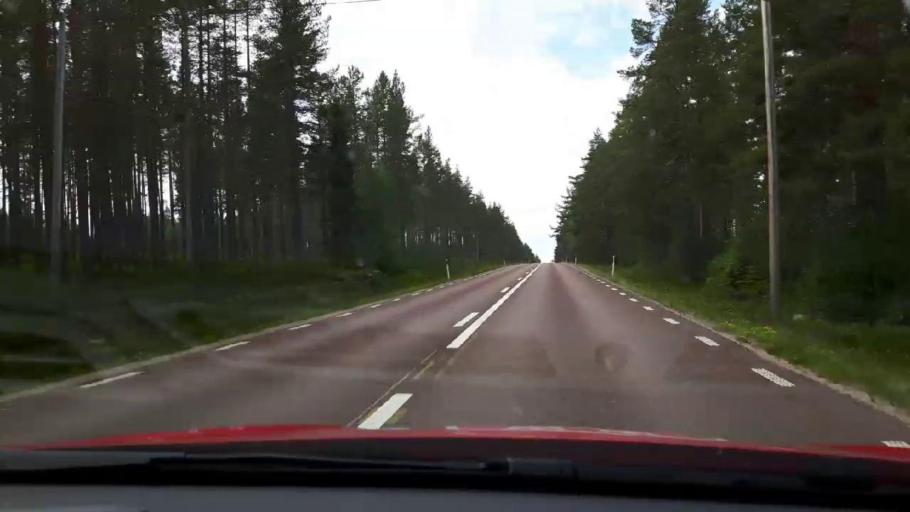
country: SE
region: Jaemtland
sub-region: Harjedalens Kommun
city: Sveg
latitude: 62.0498
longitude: 14.5034
